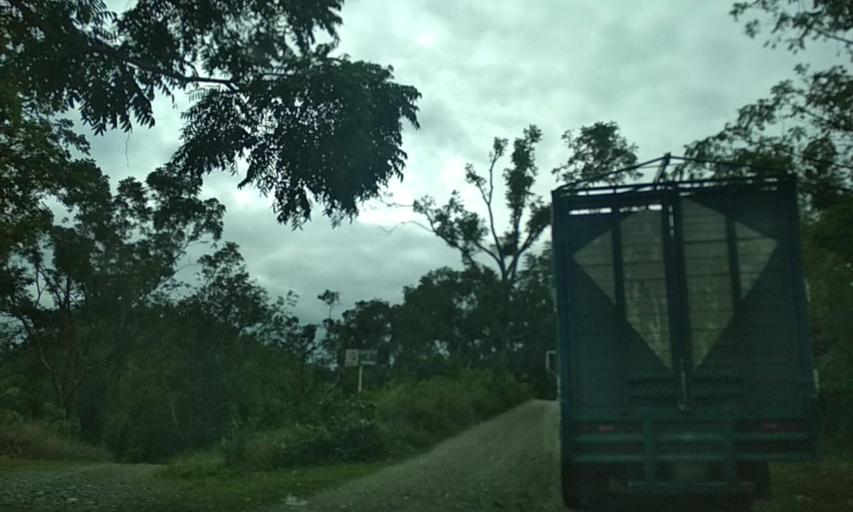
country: MX
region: Veracruz
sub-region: Papantla
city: Residencial Tajin
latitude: 20.6268
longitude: -97.3638
